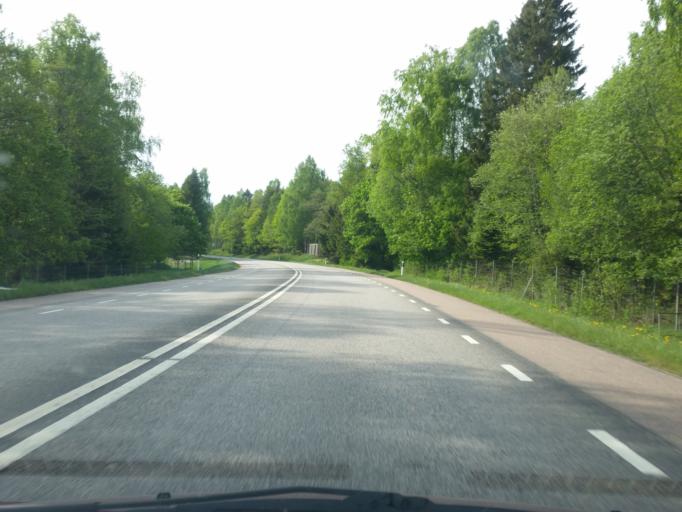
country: SE
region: Vaestra Goetaland
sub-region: Ulricehamns Kommun
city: Ulricehamn
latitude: 57.8110
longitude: 13.2959
